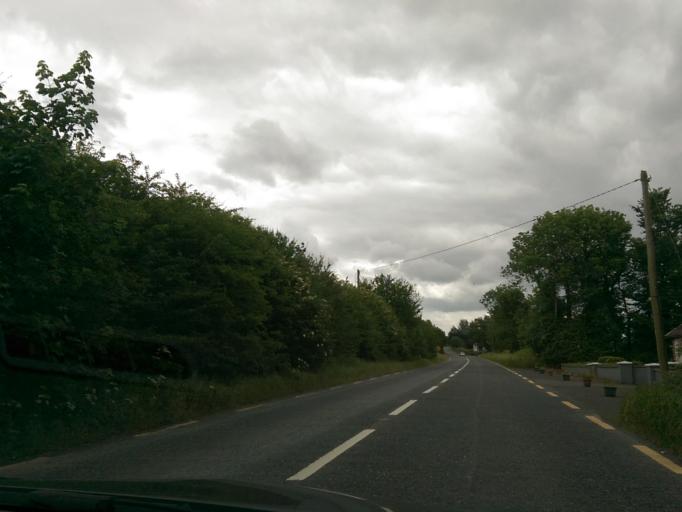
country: IE
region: Munster
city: Thurles
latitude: 52.6491
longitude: -7.7960
